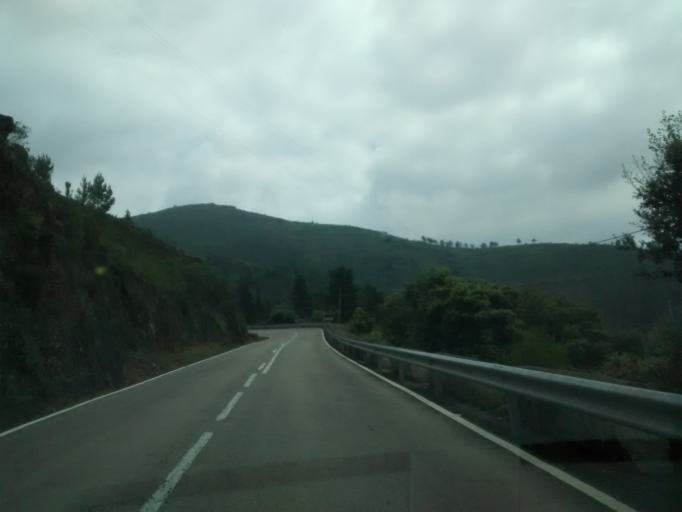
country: ES
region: Galicia
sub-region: Provincia de Ourense
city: Manzaneda
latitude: 42.3323
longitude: -7.2024
